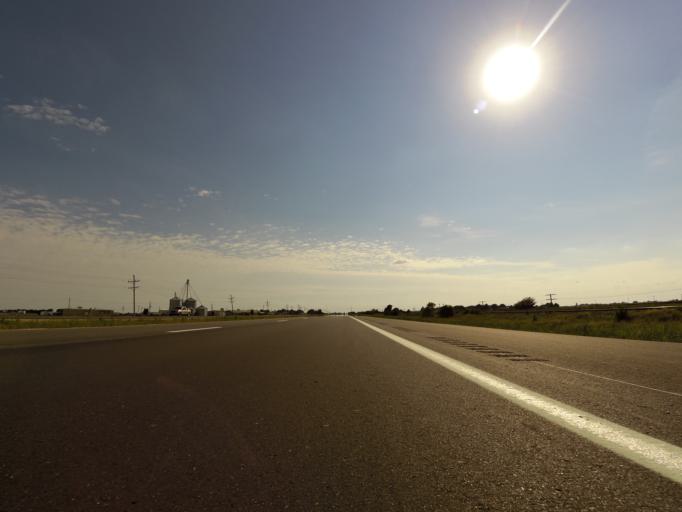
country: US
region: Kansas
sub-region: Reno County
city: South Hutchinson
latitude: 38.0018
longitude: -98.0246
